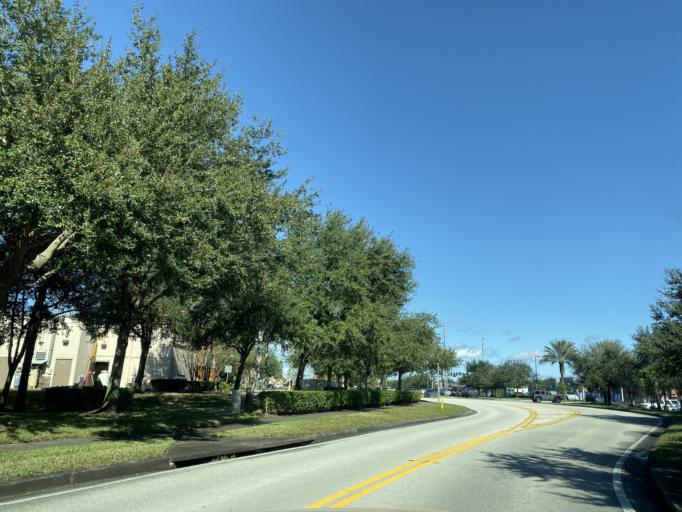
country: US
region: Florida
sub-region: Seminole County
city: Goldenrod
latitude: 28.6169
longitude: -81.2620
